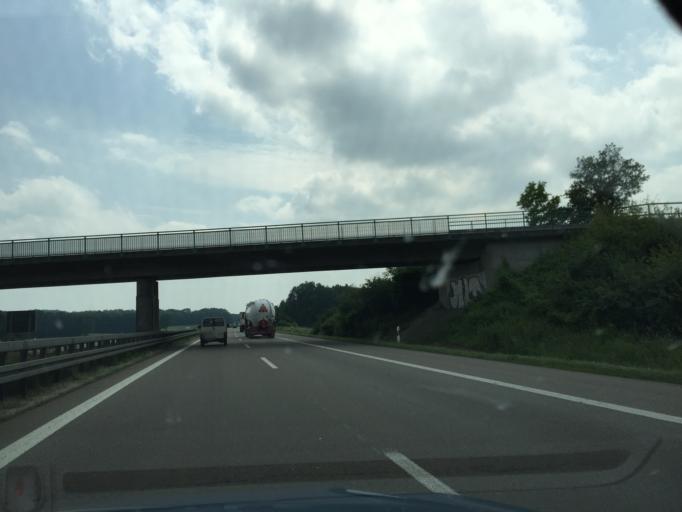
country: DE
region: Bavaria
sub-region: Swabia
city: Holzheim
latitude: 48.4022
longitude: 10.0921
